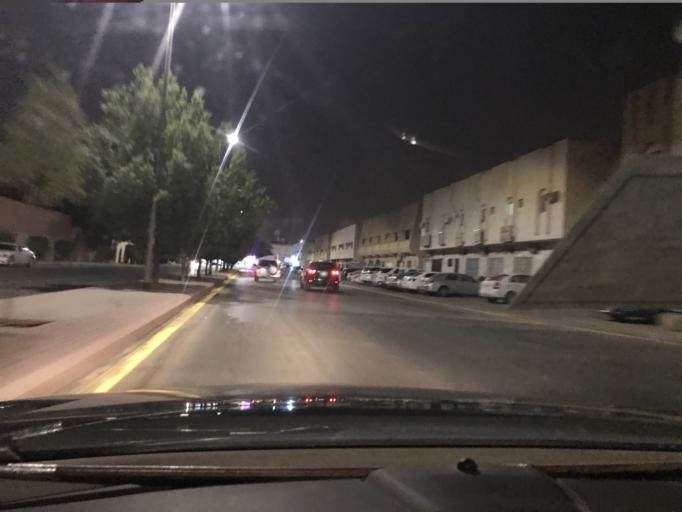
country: SA
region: Ar Riyad
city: Riyadh
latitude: 24.7383
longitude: 46.7721
